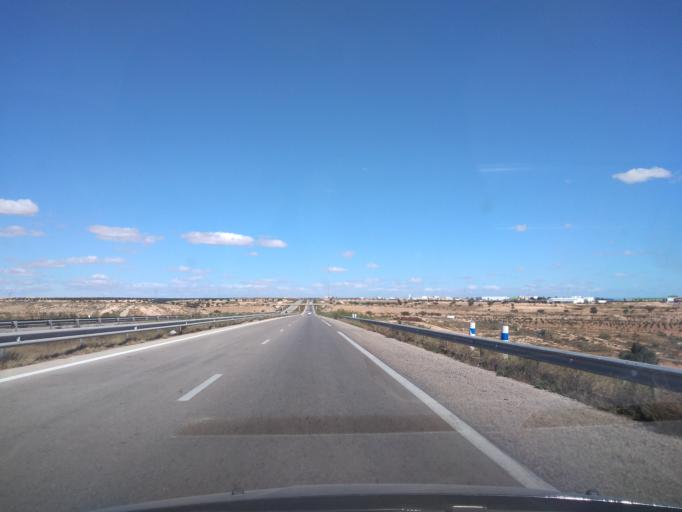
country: TN
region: Safaqis
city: Al Qarmadah
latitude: 34.9215
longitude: 10.7377
